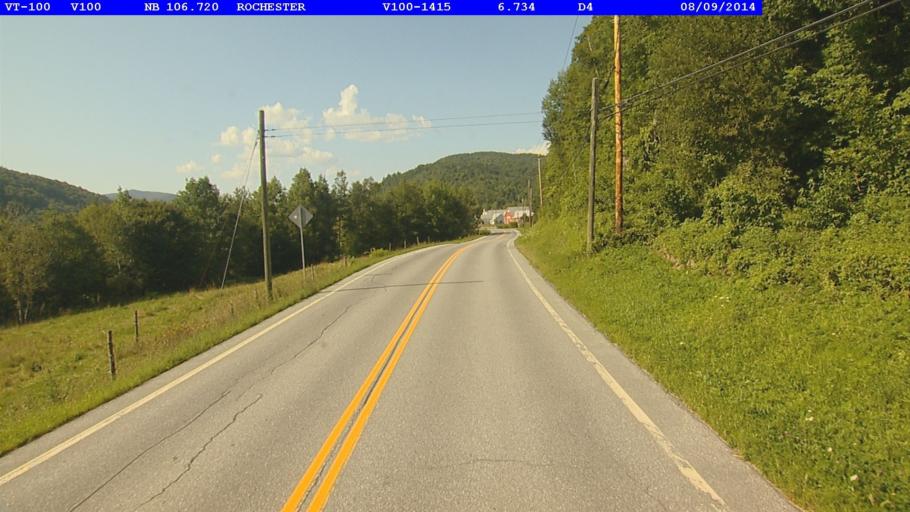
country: US
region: Vermont
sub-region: Orange County
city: Randolph
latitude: 43.8920
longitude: -72.8184
